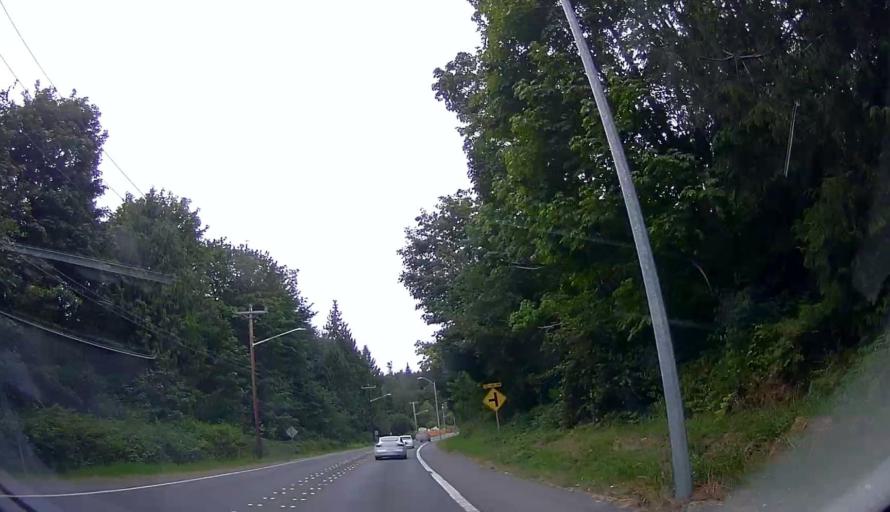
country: US
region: Washington
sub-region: Snohomish County
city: Tulalip
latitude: 48.0390
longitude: -122.2473
